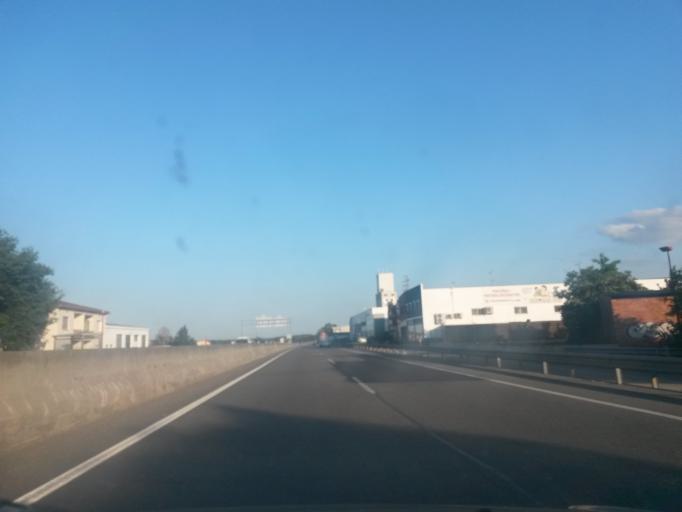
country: ES
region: Catalonia
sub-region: Provincia de Girona
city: Cornella del Terri
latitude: 42.0944
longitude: 2.8019
